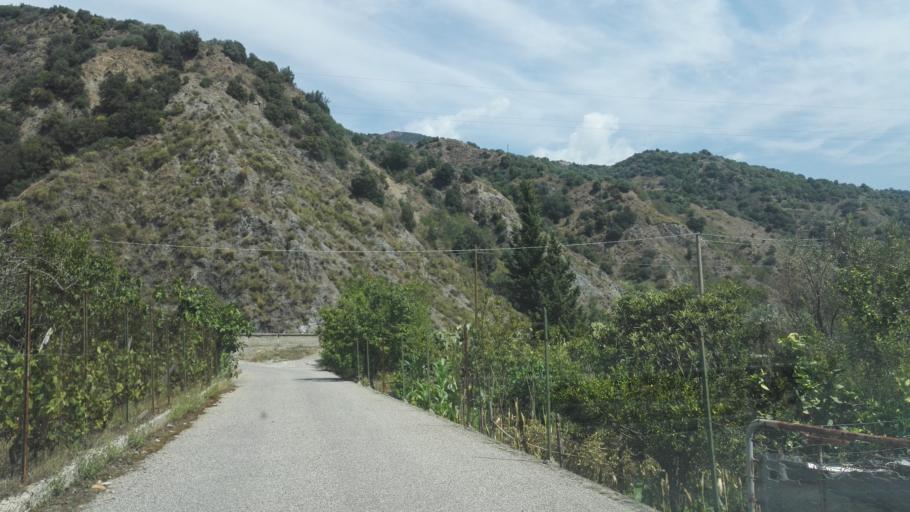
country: IT
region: Calabria
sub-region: Provincia di Reggio Calabria
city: Bivongi
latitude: 38.4830
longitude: 16.4445
